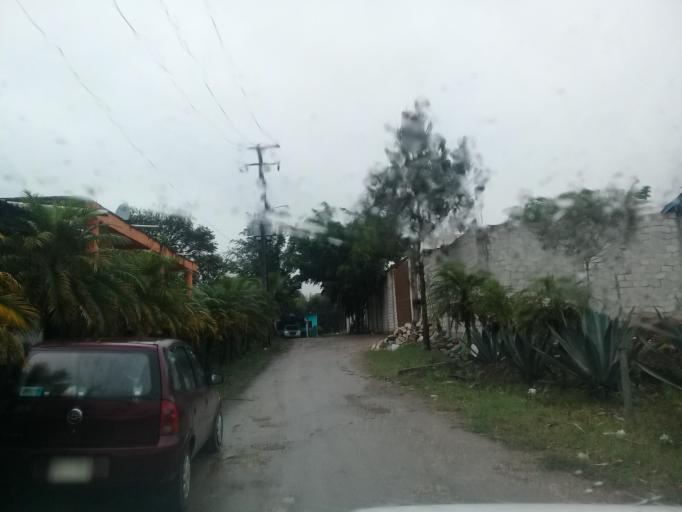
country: MX
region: Veracruz
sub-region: Cordoba
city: San Jose de Tapia
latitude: 18.8509
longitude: -96.9505
